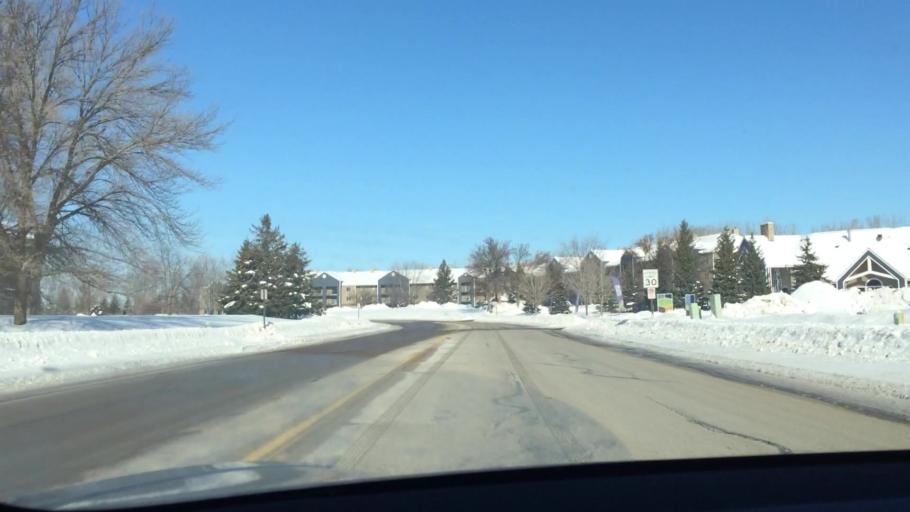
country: US
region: Minnesota
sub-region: Hennepin County
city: Plymouth
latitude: 45.0192
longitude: -93.4642
